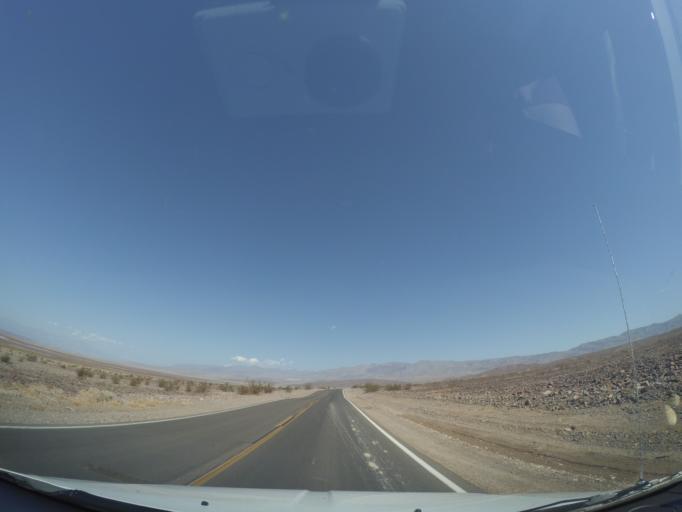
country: US
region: Nevada
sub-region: Nye County
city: Beatty
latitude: 36.5230
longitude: -116.8826
